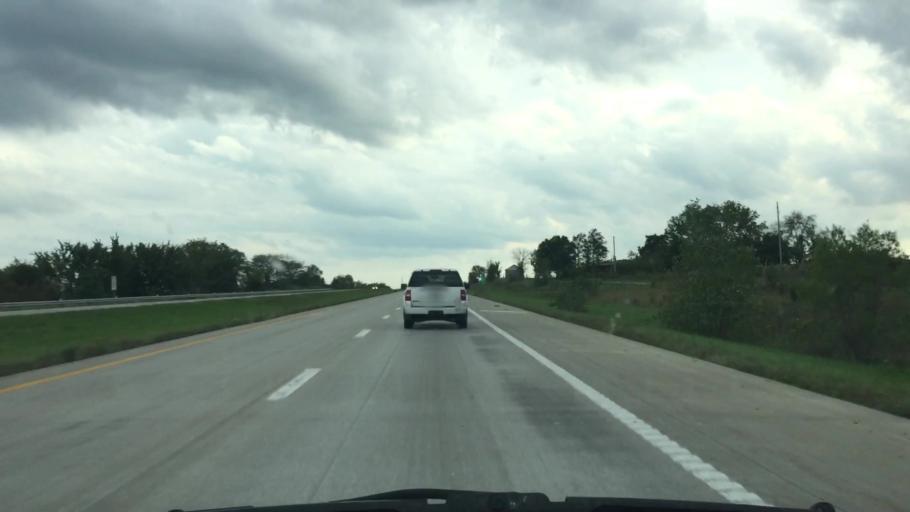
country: US
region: Missouri
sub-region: Clinton County
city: Cameron
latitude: 39.6513
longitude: -94.2400
